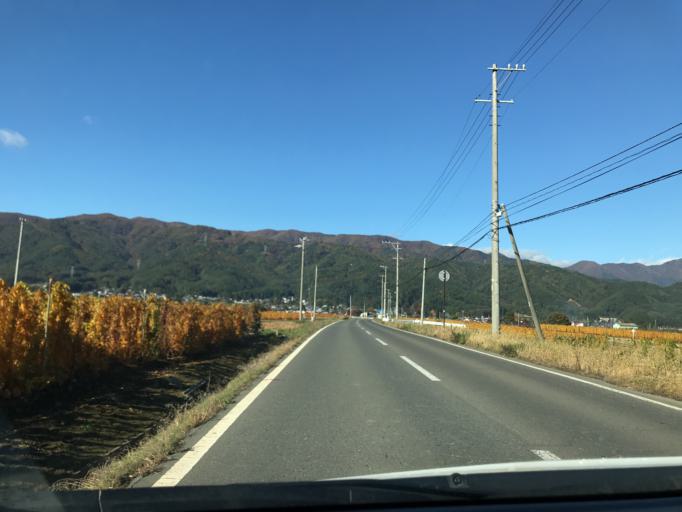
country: JP
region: Nagano
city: Shiojiri
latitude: 36.1580
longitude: 137.8853
